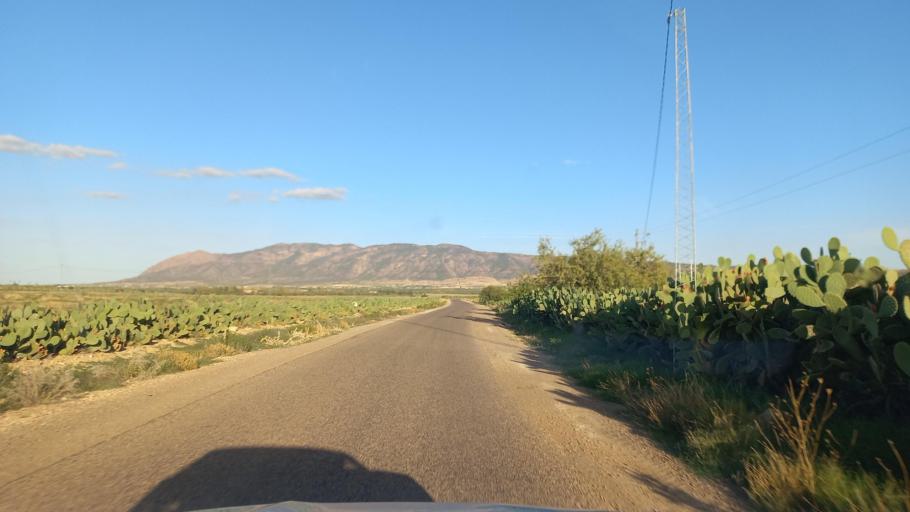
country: TN
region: Al Qasrayn
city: Sbiba
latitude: 35.4114
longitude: 9.1357
